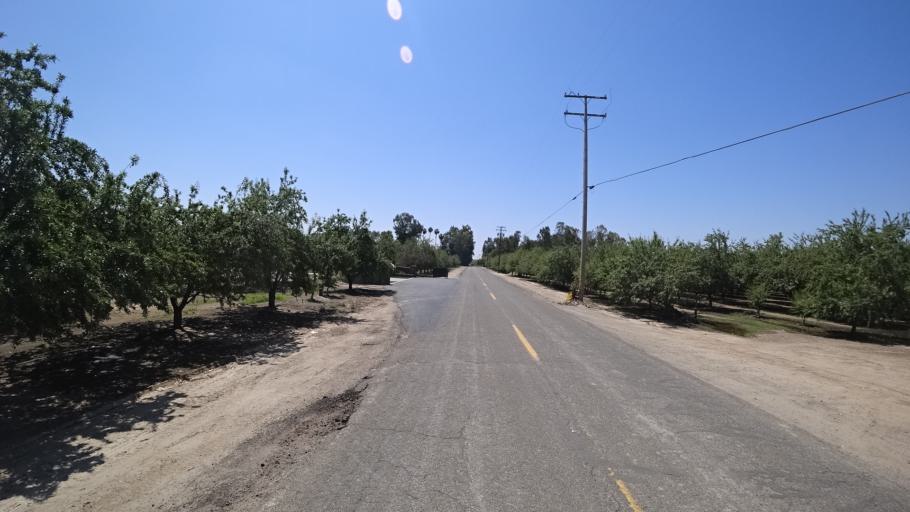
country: US
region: California
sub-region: Kings County
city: Armona
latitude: 36.2932
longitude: -119.6912
